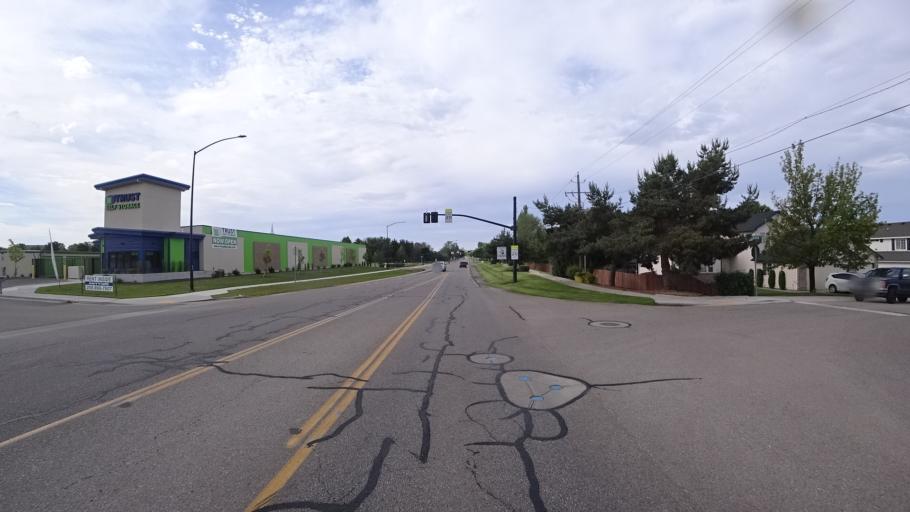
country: US
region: Idaho
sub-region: Ada County
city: Meridian
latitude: 43.5887
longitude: -116.3746
